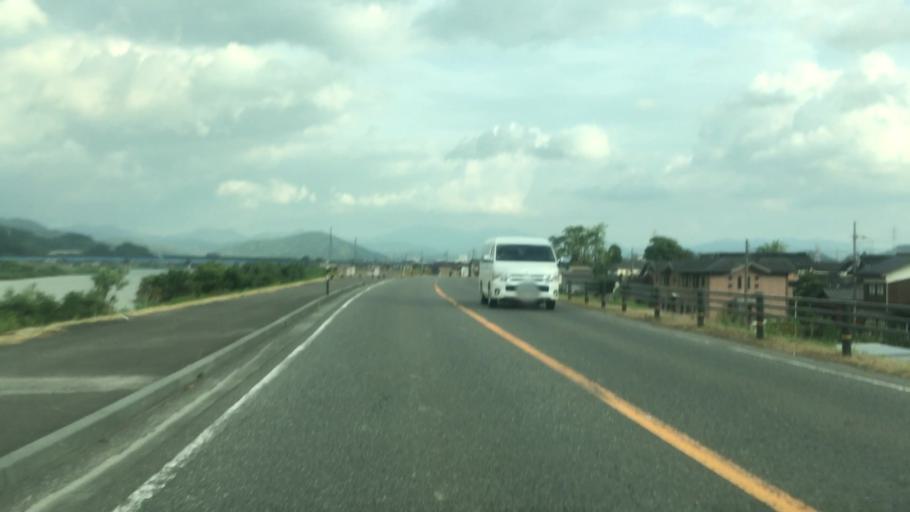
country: JP
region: Hyogo
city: Toyooka
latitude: 35.5617
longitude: 134.8138
